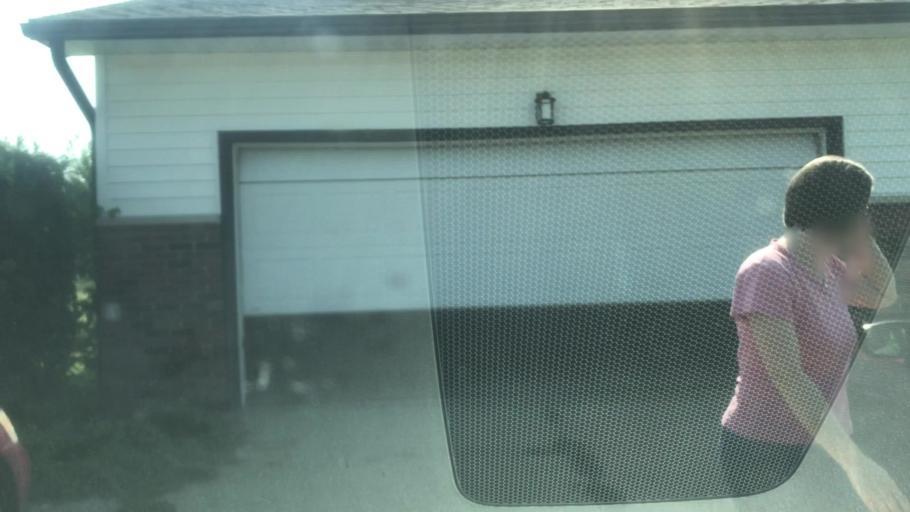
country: US
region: Nebraska
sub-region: Hall County
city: Grand Island
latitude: 40.8924
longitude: -98.3055
